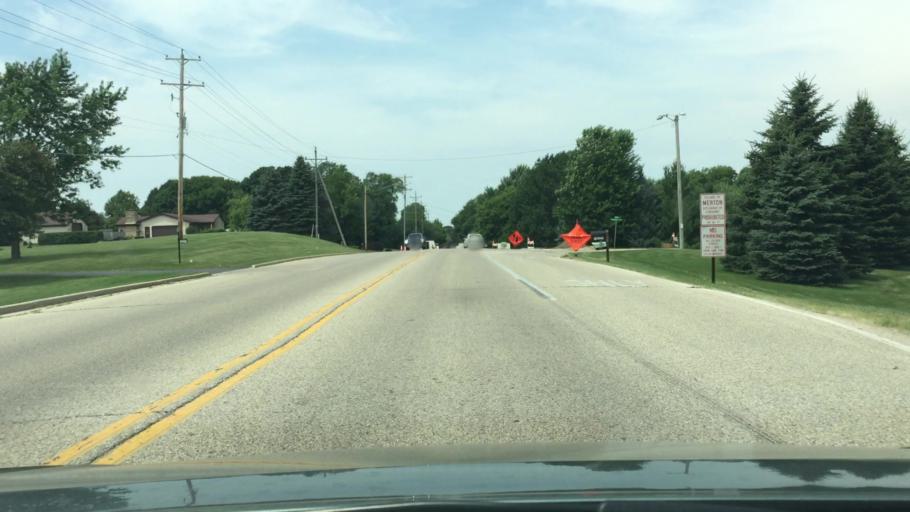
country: US
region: Wisconsin
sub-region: Waukesha County
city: Merton
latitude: 43.1413
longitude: -88.3024
